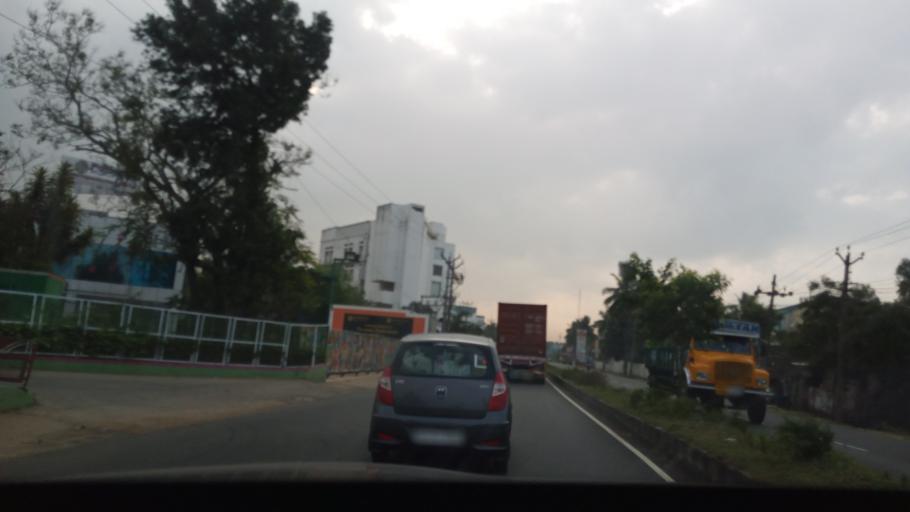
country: IN
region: Tamil Nadu
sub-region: Kancheepuram
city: Vengavasal
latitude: 12.8305
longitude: 80.1621
